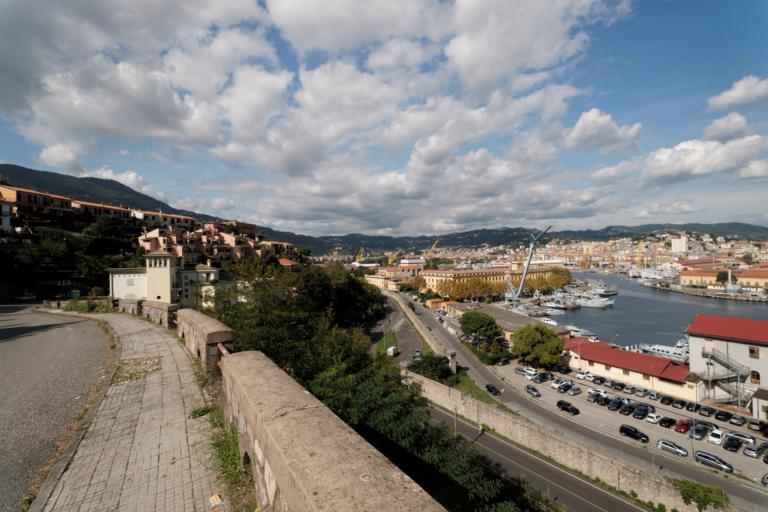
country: IT
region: Liguria
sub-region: Provincia di La Spezia
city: La Spezia
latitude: 44.0948
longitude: 9.8146
